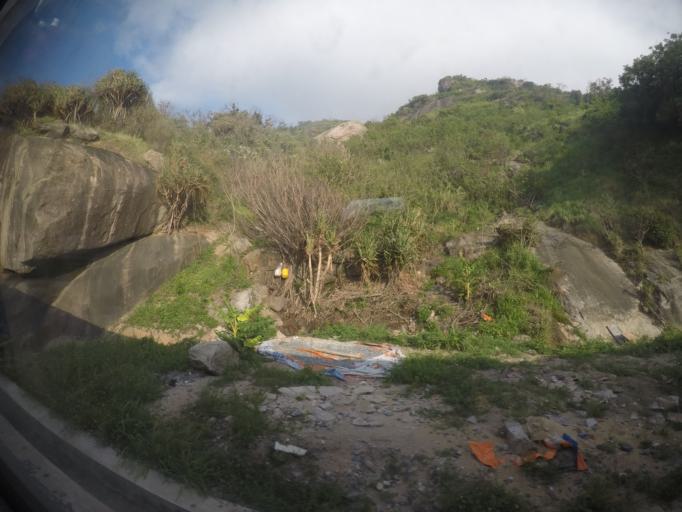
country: VN
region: Khanh Hoa
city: Van Gia
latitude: 12.8567
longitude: 109.4010
